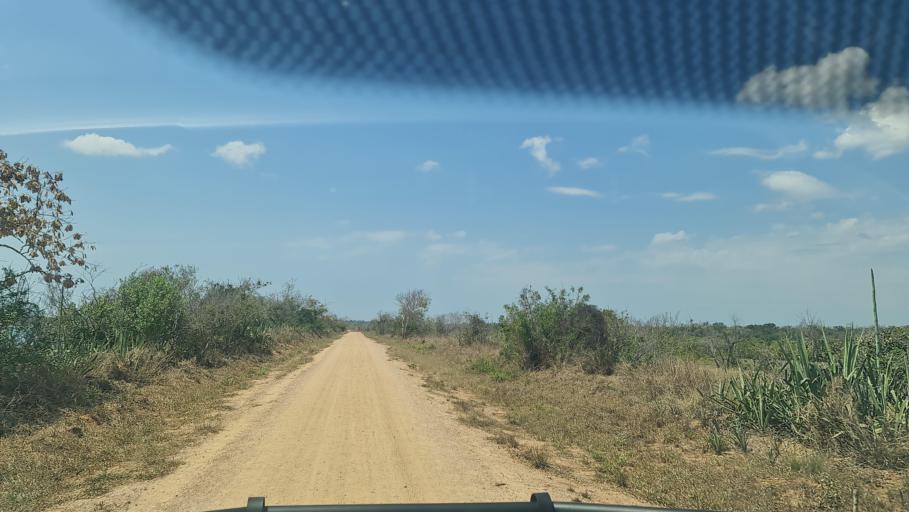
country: MZ
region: Nampula
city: Ilha de Mocambique
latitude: -15.1821
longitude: 40.5161
